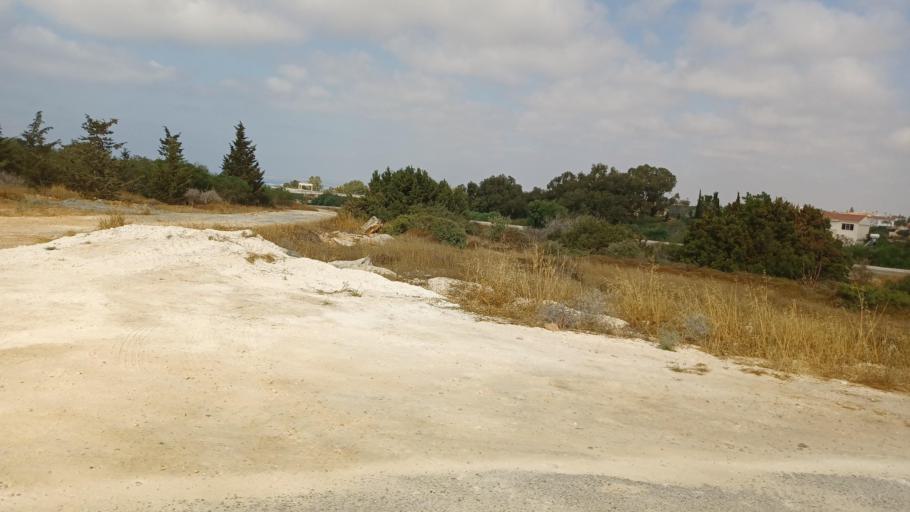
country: CY
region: Ammochostos
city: Ayia Napa
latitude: 34.9997
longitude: 34.0121
